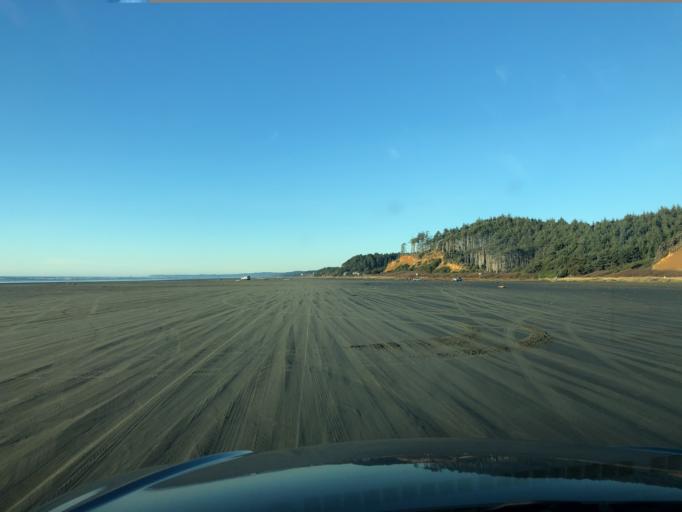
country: US
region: Washington
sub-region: Grays Harbor County
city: Ocean Shores
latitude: 47.1728
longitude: -124.1967
